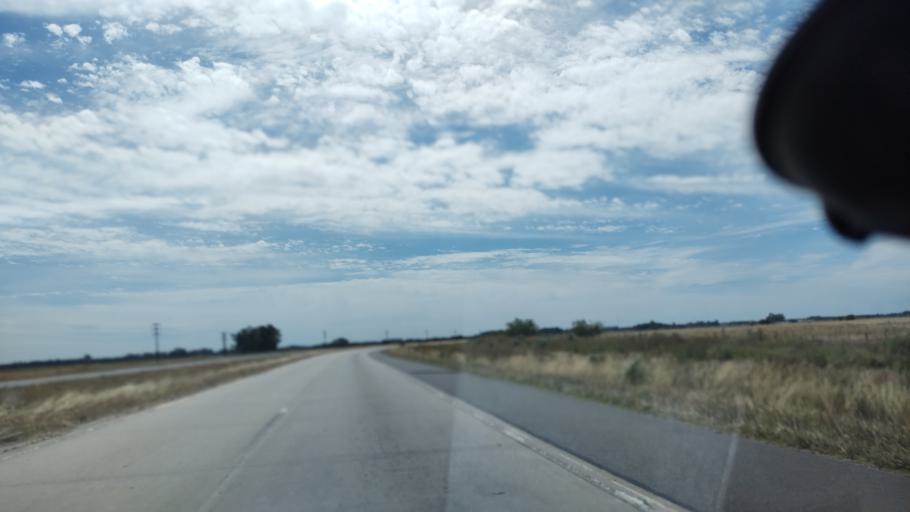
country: AR
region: Buenos Aires
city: Canuelas
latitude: -35.0727
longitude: -58.6948
